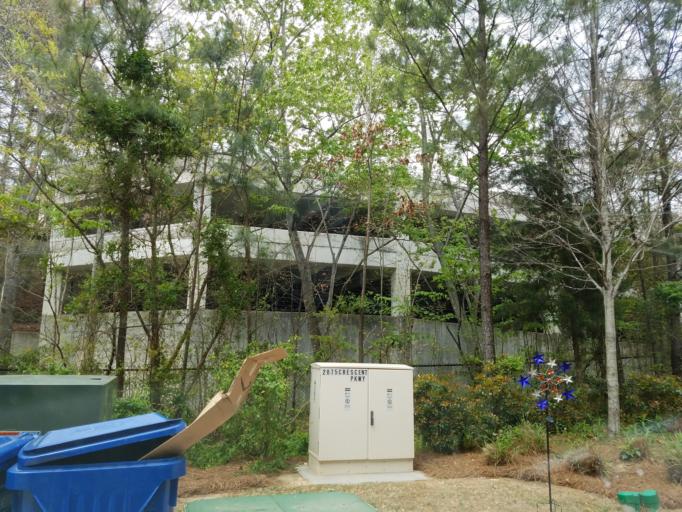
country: US
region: Georgia
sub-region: Cobb County
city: Vinings
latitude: 33.8945
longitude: -84.4694
